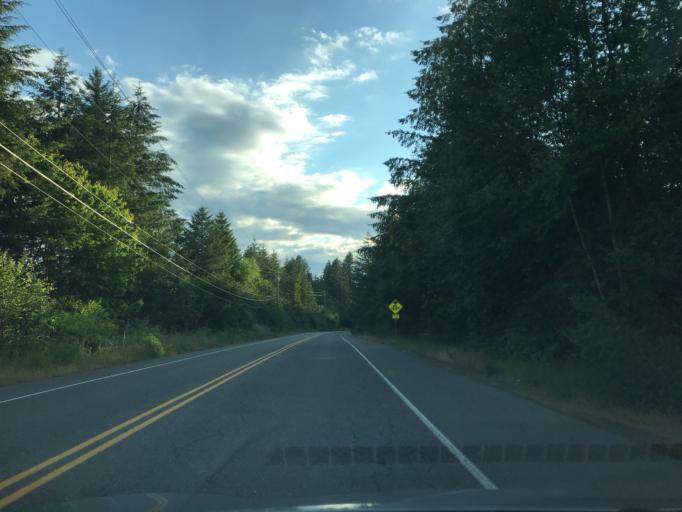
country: US
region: Washington
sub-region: King County
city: Black Diamond
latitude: 47.3111
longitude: -122.0353
